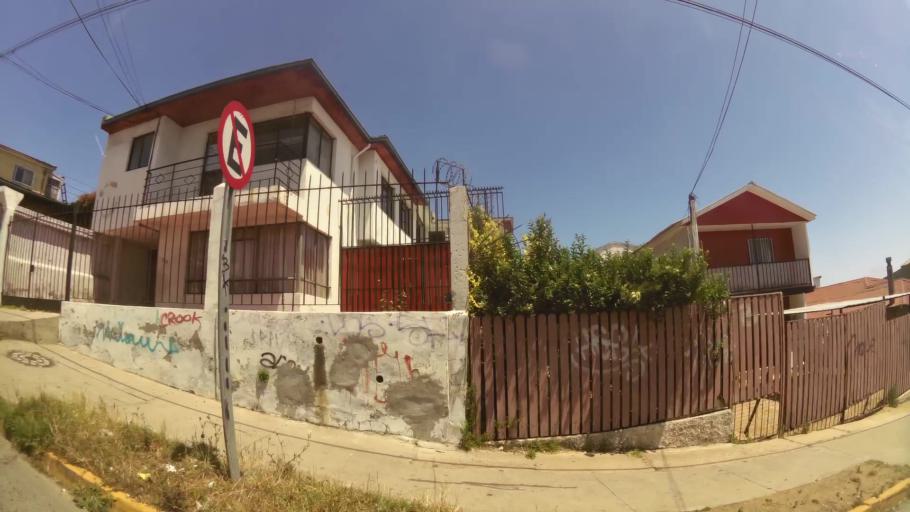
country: CL
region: Valparaiso
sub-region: Provincia de Valparaiso
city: Valparaiso
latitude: -33.0352
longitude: -71.6423
